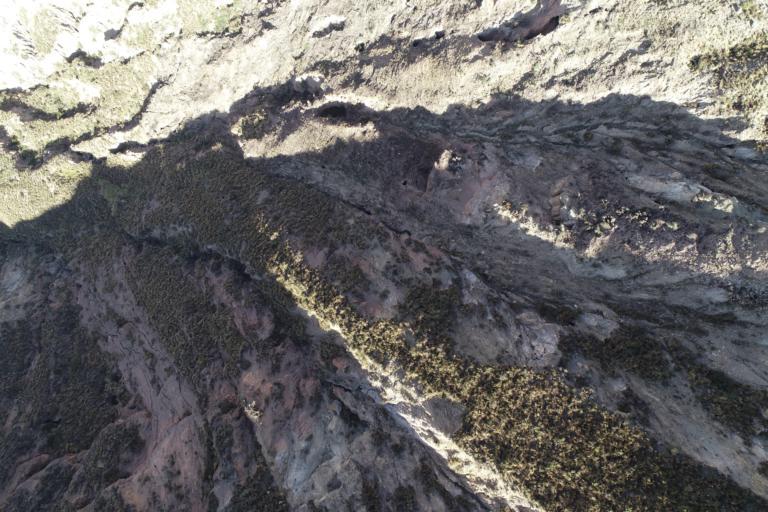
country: BO
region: La Paz
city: La Paz
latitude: -16.5502
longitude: -68.1056
